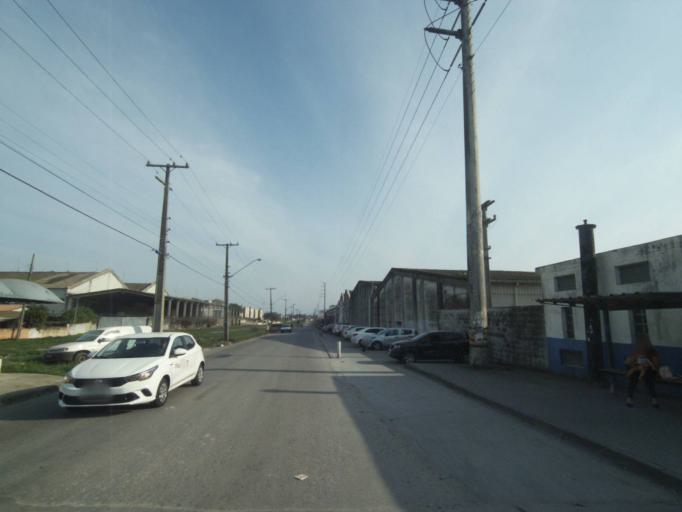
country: BR
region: Parana
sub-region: Paranagua
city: Paranagua
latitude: -25.5292
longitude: -48.5307
